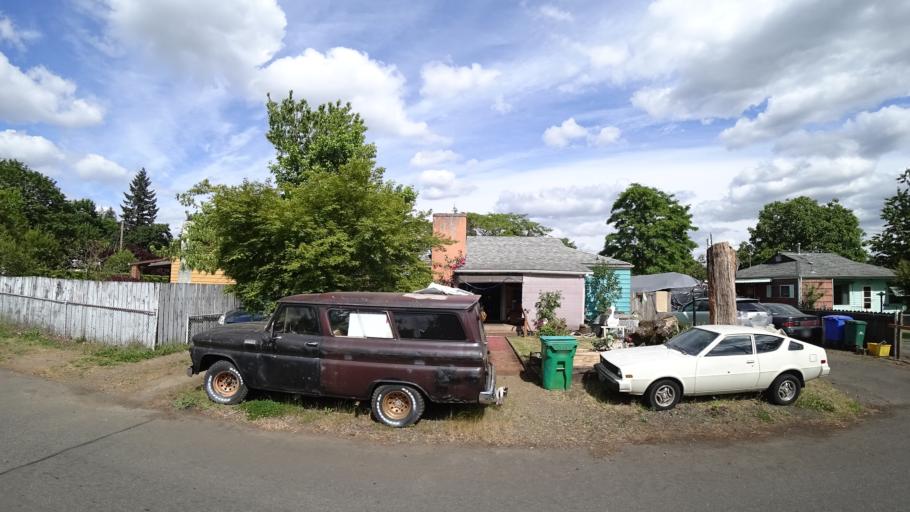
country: US
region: Oregon
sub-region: Multnomah County
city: Lents
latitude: 45.4912
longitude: -122.5446
